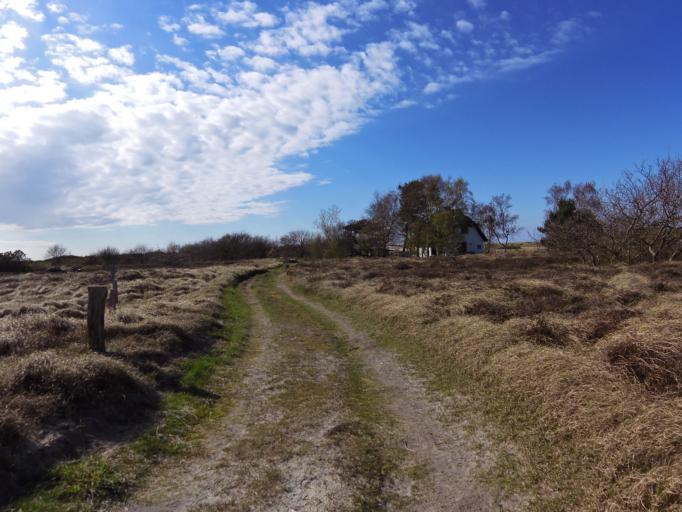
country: DE
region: Mecklenburg-Vorpommern
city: Hiddensee
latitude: 54.5567
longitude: 13.1006
